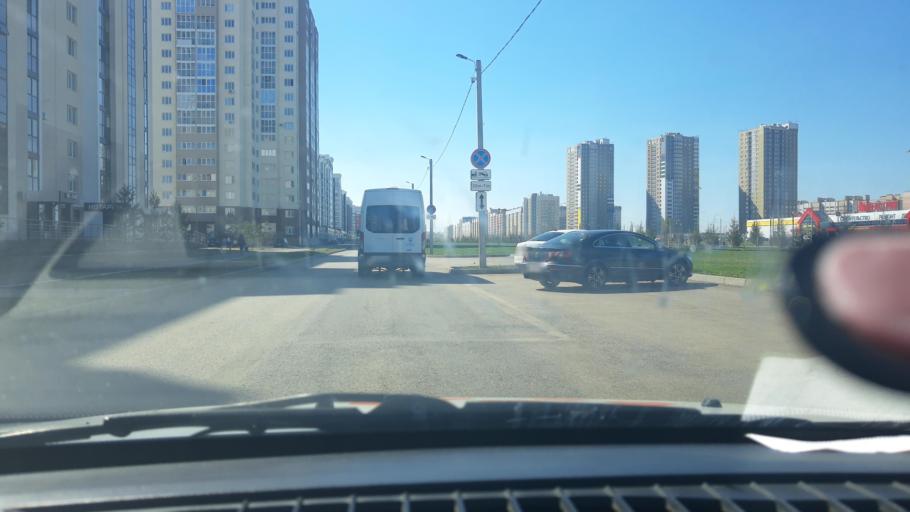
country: RU
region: Bashkortostan
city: Sterlitamak
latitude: 53.6292
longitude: 55.9024
